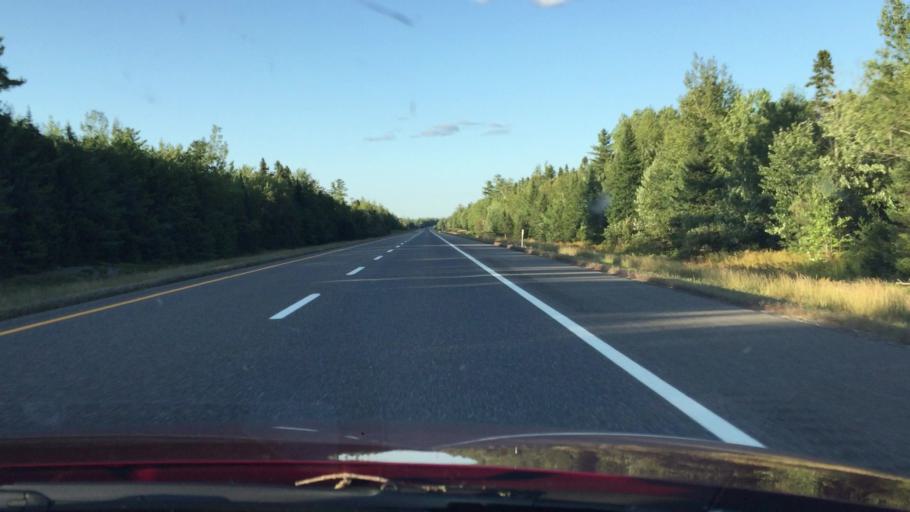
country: US
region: Maine
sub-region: Penobscot County
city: Patten
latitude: 46.0719
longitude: -68.2216
